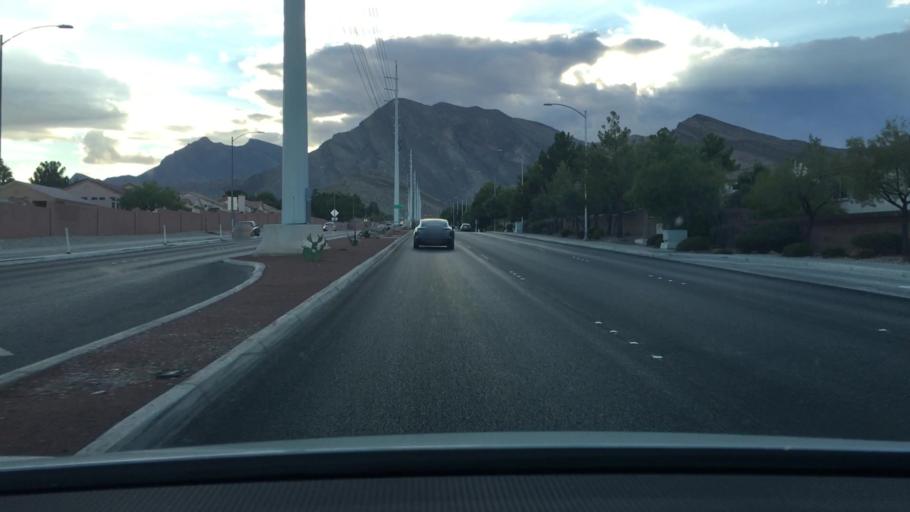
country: US
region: Nevada
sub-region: Clark County
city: Summerlin South
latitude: 36.2183
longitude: -115.3163
